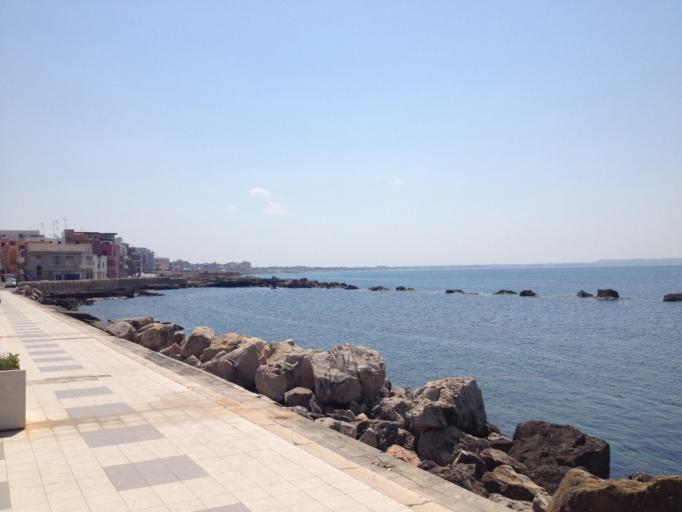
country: IT
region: Apulia
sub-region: Provincia di Lecce
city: Gallipoli
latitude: 40.0550
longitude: 17.9831
